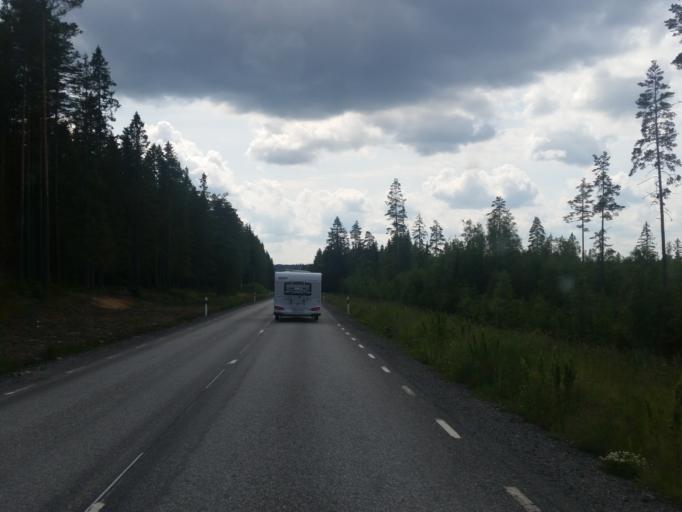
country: SE
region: OErebro
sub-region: Ljusnarsbergs Kommun
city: Kopparberg
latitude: 59.9608
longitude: 15.0208
